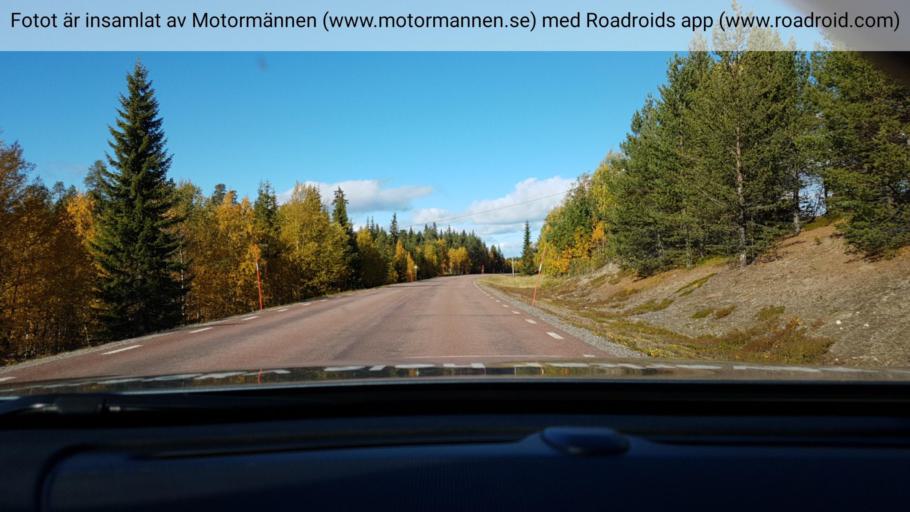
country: SE
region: Norrbotten
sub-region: Arjeplogs Kommun
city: Arjeplog
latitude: 66.0123
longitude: 18.0888
